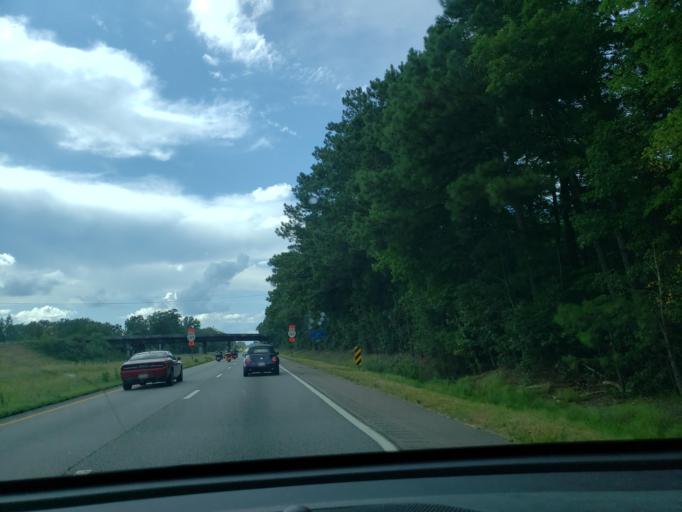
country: US
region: Virginia
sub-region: City of Franklin
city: Franklin
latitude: 36.6471
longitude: -76.9100
